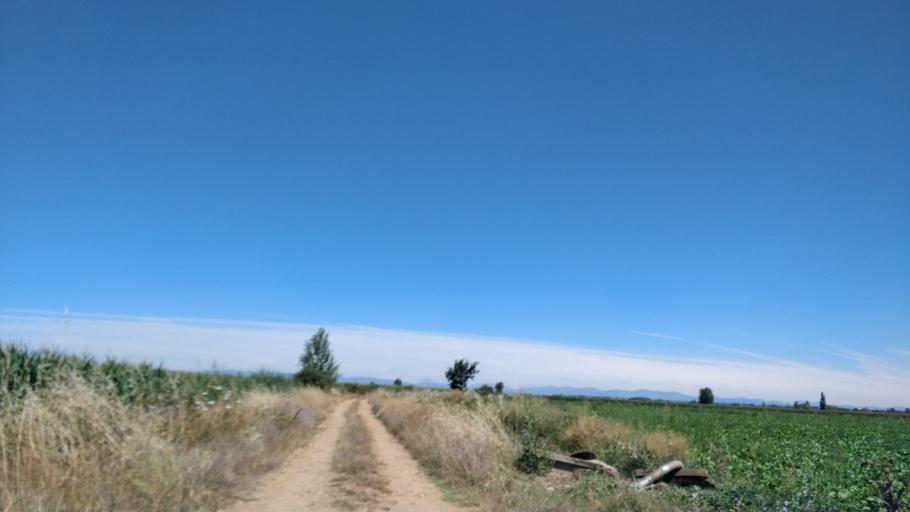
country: ES
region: Castille and Leon
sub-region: Provincia de Leon
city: Bustillo del Paramo
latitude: 42.4448
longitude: -5.8151
